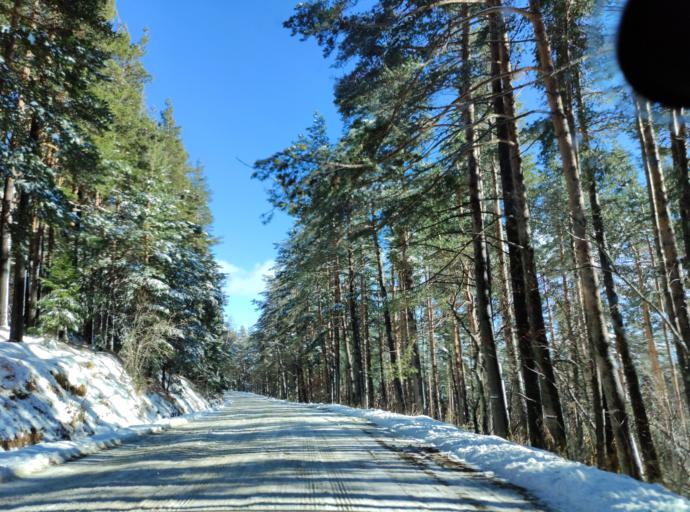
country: BG
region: Sofia-Capital
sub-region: Stolichna Obshtina
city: Sofia
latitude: 42.5883
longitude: 23.3068
